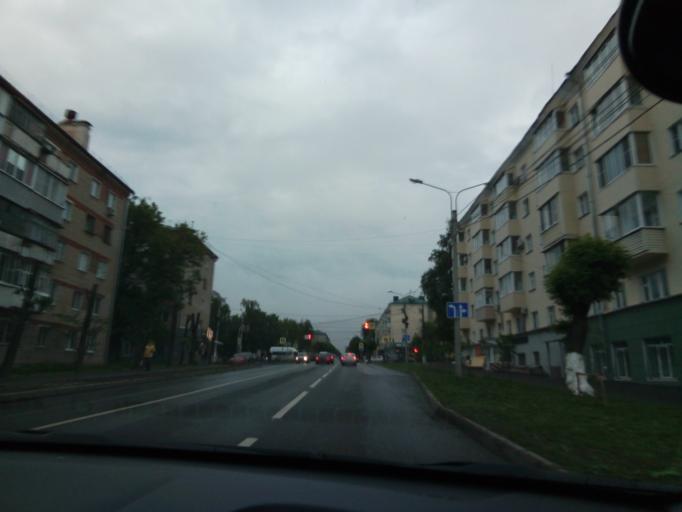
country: RU
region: Chuvashia
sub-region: Cheboksarskiy Rayon
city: Cheboksary
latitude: 56.1252
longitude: 47.2556
